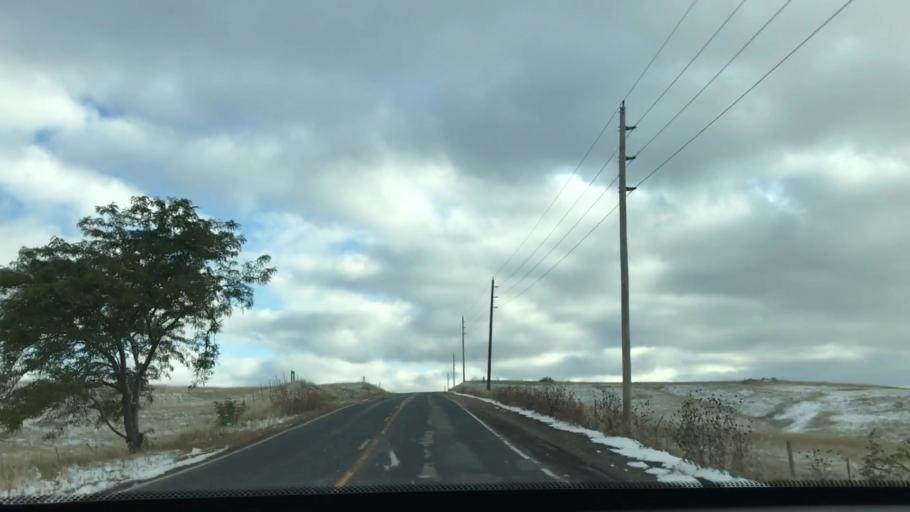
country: US
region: Colorado
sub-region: Boulder County
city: Lafayette
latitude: 39.9629
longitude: -105.0719
